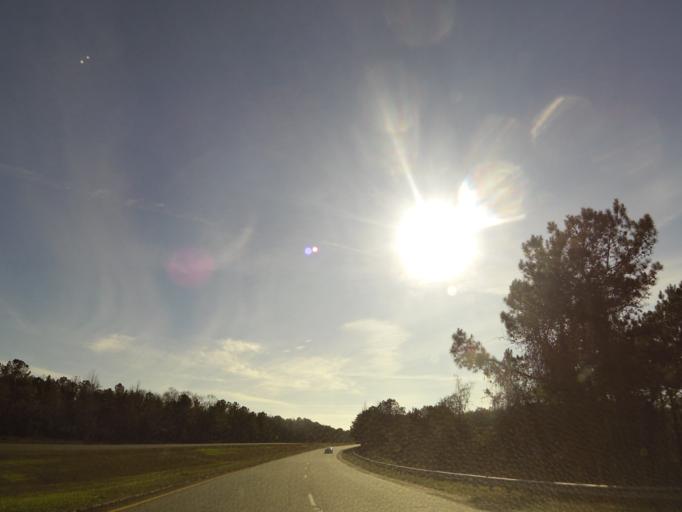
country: US
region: Georgia
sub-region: Stewart County
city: Richland
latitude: 32.1808
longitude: -84.7012
